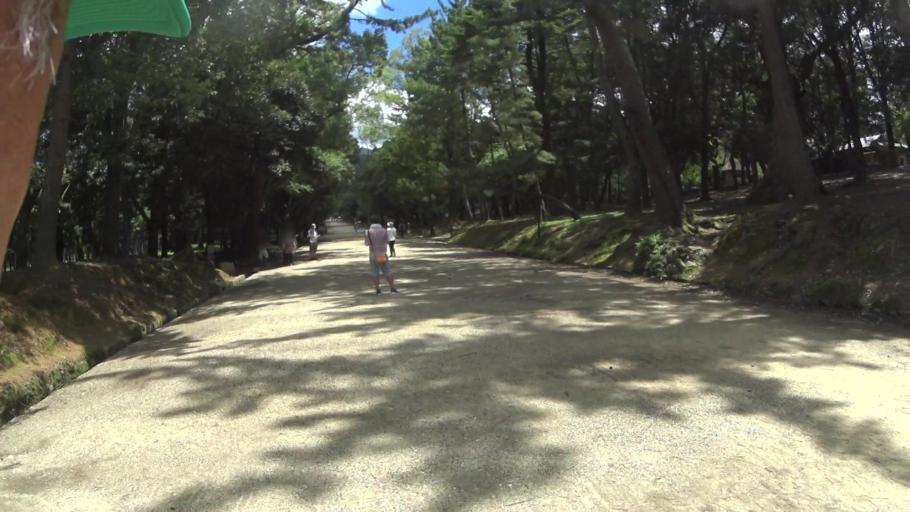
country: JP
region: Nara
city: Nara-shi
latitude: 34.6821
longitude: 135.8353
